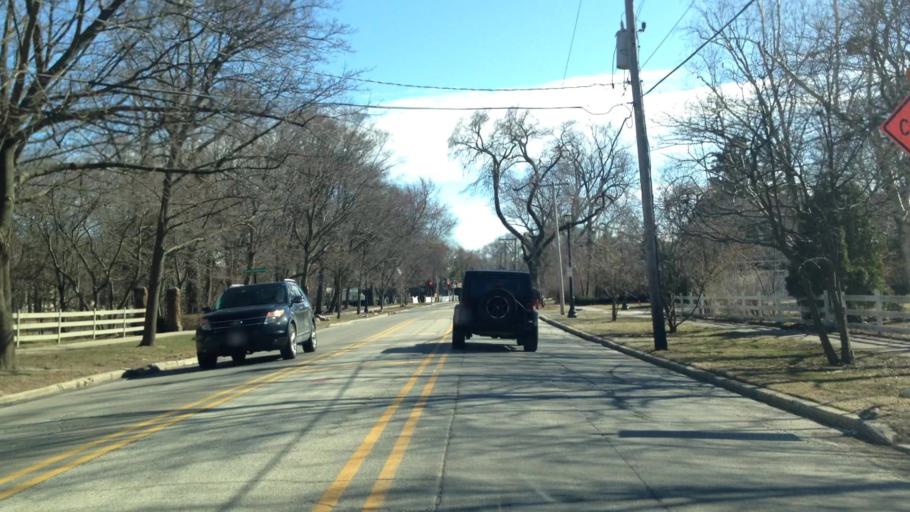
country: US
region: Illinois
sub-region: Cook County
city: Evanston
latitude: 42.0658
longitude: -87.6778
